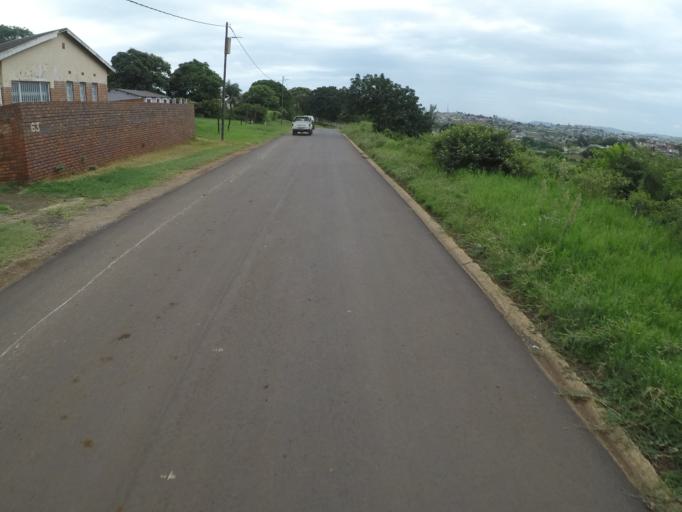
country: ZA
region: KwaZulu-Natal
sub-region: uThungulu District Municipality
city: Empangeni
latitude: -28.7704
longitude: 31.8615
